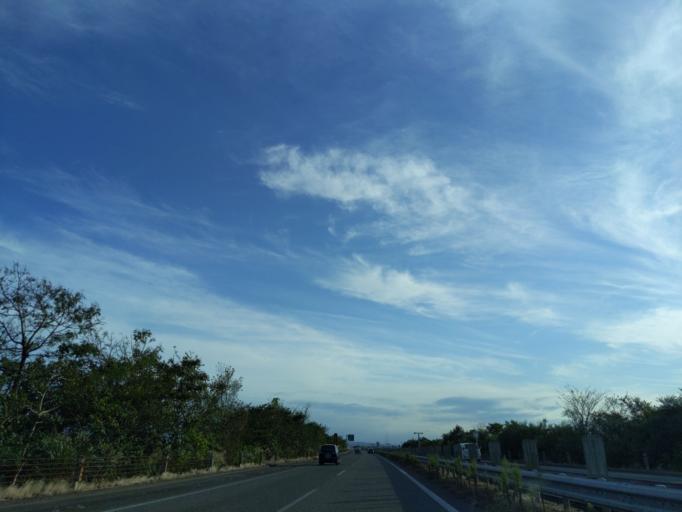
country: JP
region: Niigata
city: Nagaoka
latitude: 37.4885
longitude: 138.8263
